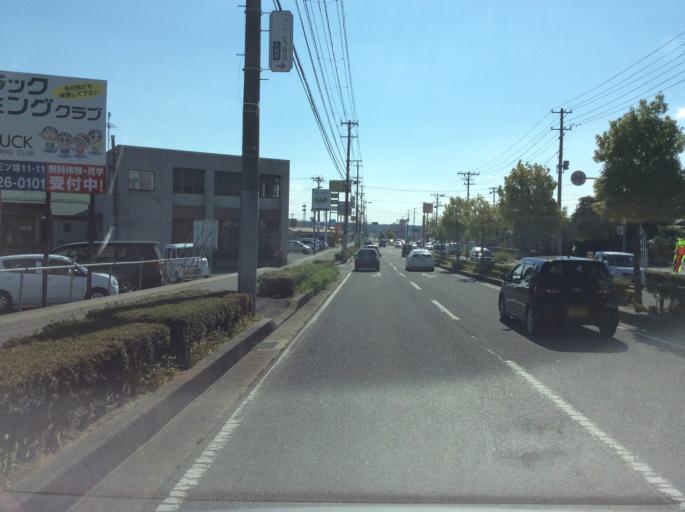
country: JP
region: Fukushima
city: Koriyama
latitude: 37.3789
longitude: 140.3582
